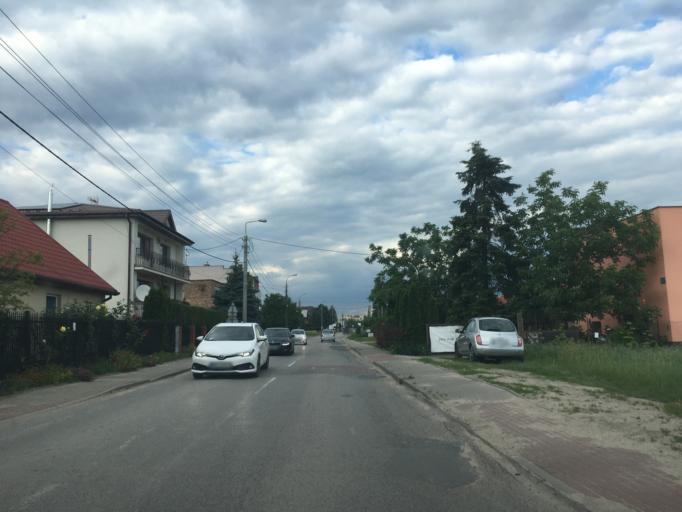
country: PL
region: Masovian Voivodeship
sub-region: Powiat piaseczynski
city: Mysiadlo
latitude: 52.1089
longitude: 20.9815
